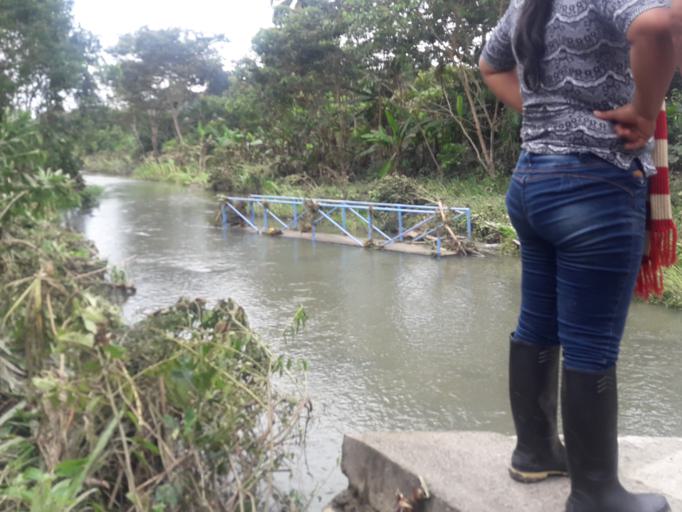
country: EC
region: Napo
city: Tena
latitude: -1.0421
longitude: -77.7577
